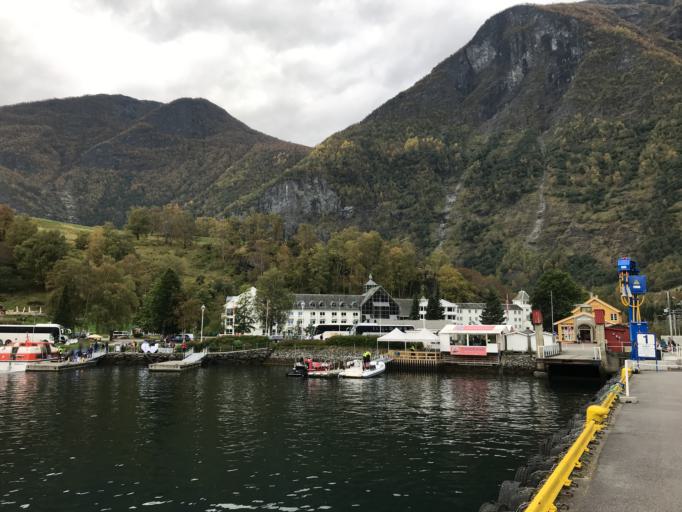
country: NO
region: Sogn og Fjordane
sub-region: Aurland
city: Aurlandsvangen
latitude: 60.8629
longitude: 7.1154
